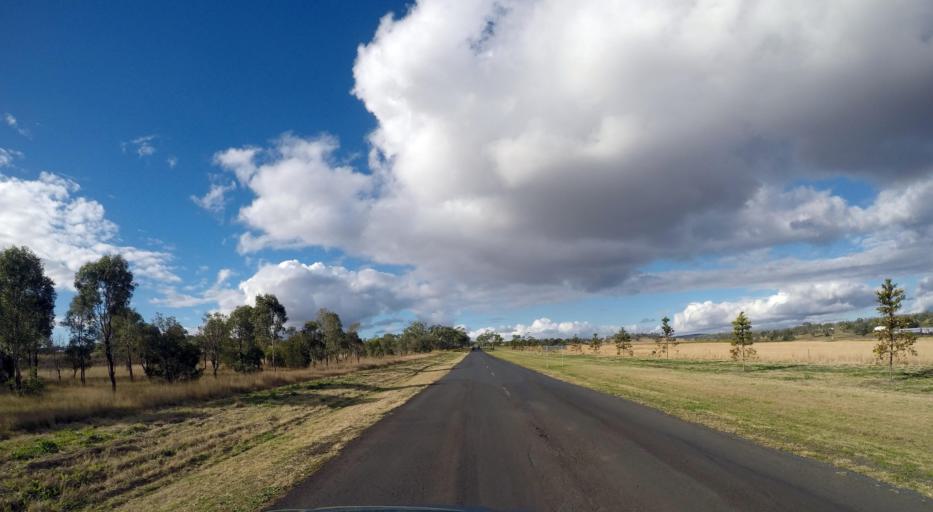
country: AU
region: Queensland
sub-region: Toowoomba
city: Westbrook
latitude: -27.7069
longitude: 151.6497
